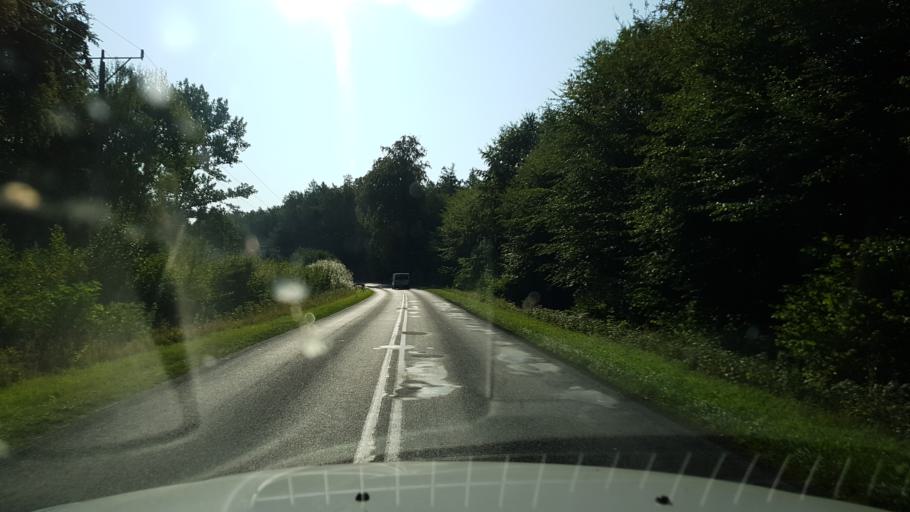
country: PL
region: West Pomeranian Voivodeship
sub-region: Powiat lobeski
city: Resko
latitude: 53.7798
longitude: 15.3421
